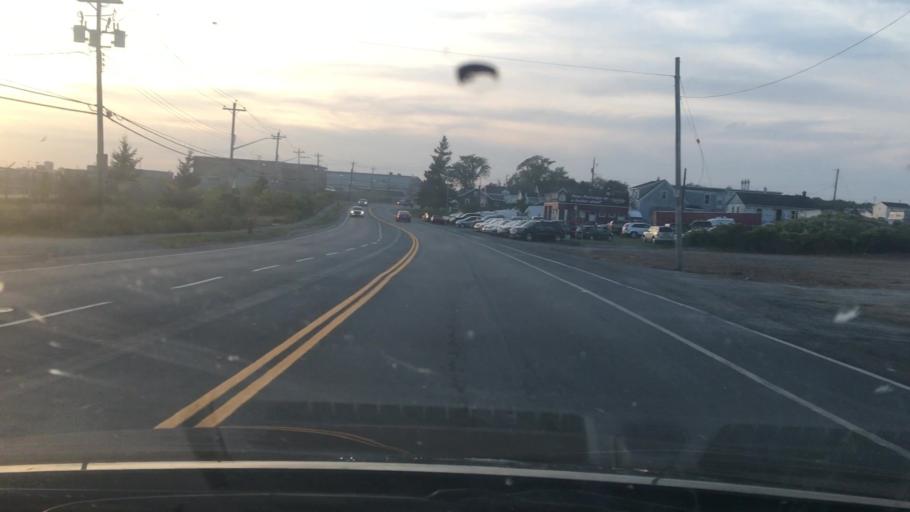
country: CA
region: Nova Scotia
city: Cole Harbour
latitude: 44.6238
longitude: -63.5107
